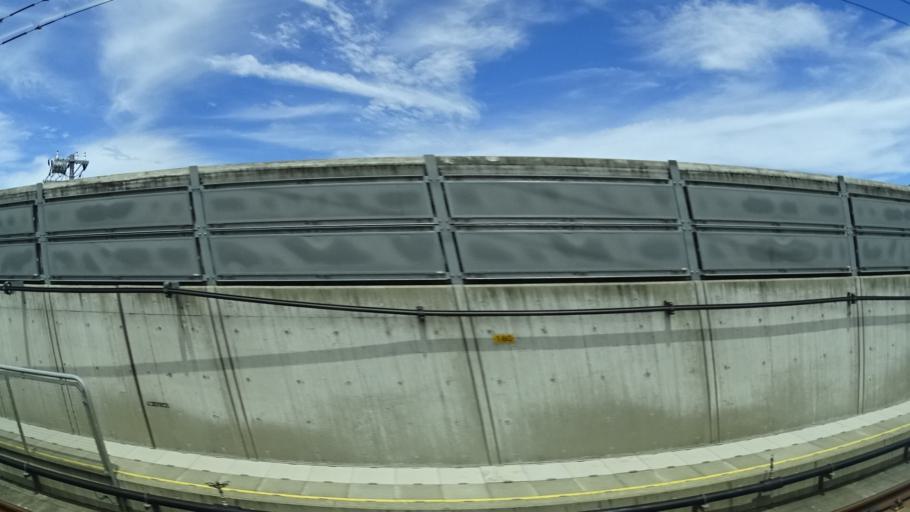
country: JP
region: Niigata
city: Itoigawa
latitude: 37.0829
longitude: 137.9930
